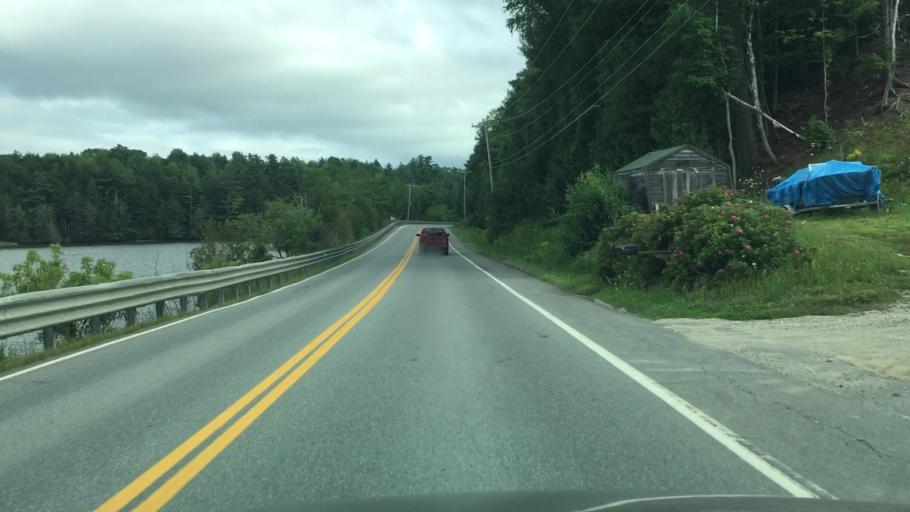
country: US
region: Maine
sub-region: Waldo County
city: Frankfort
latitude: 44.6037
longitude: -68.8699
